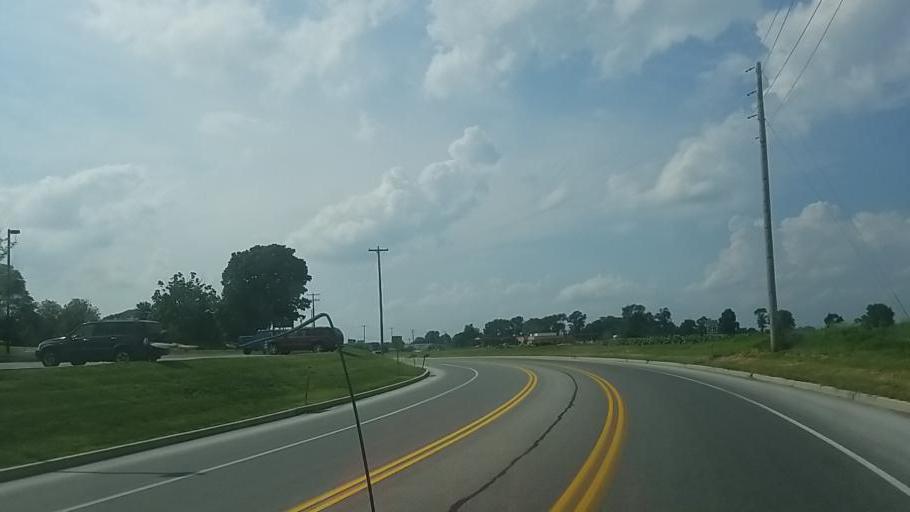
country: US
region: Pennsylvania
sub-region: Lancaster County
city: Strasburg
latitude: 39.9858
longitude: -76.1730
